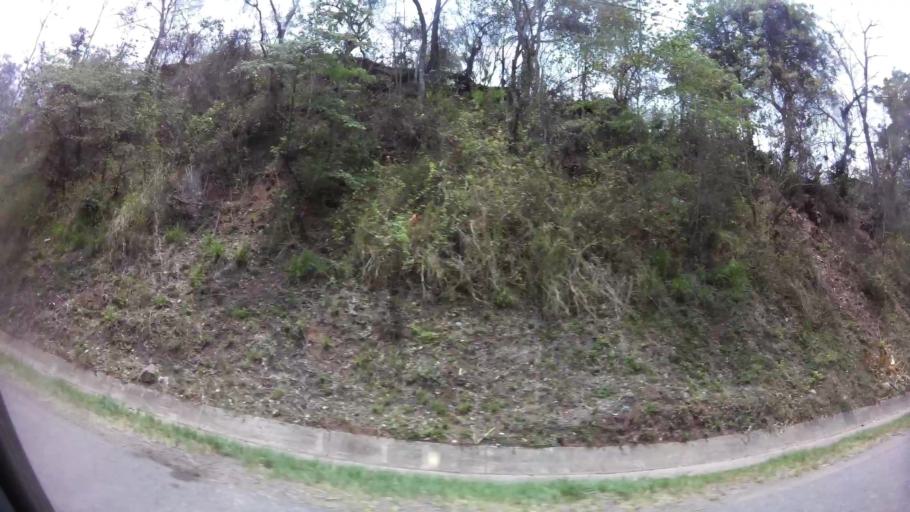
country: HN
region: Comayagua
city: Taulabe
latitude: 14.7025
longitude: -87.9634
